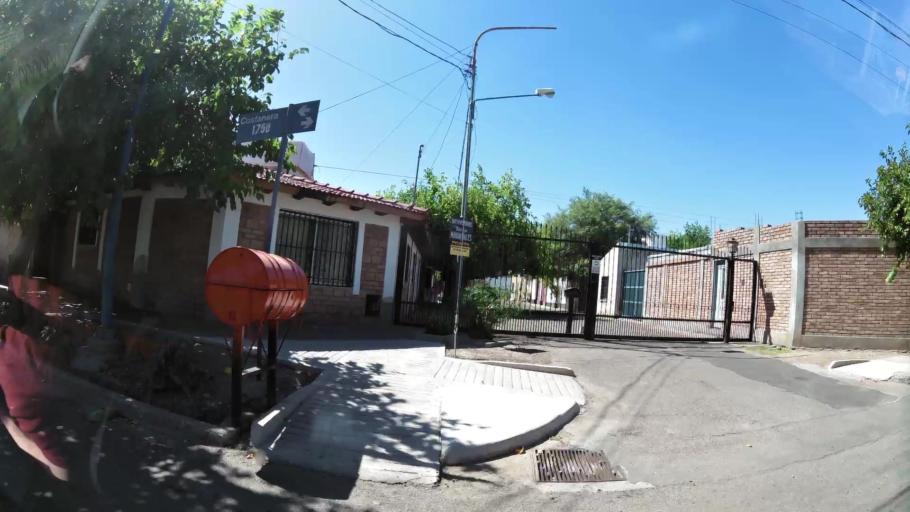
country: AR
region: Mendoza
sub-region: Departamento de Godoy Cruz
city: Godoy Cruz
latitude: -32.9473
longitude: -68.8448
